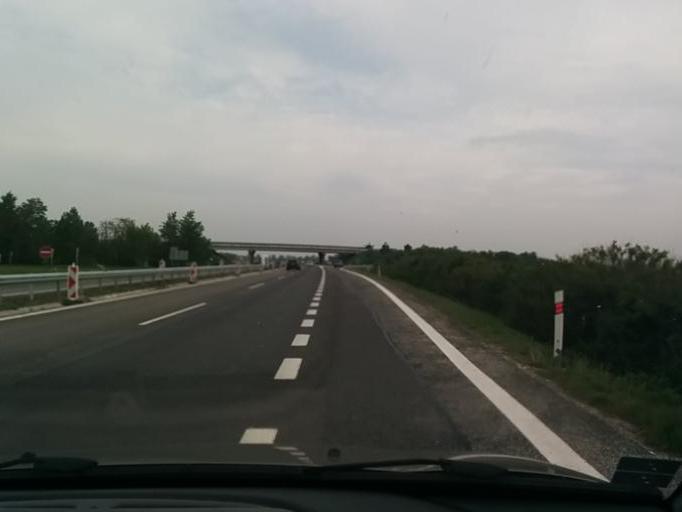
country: SK
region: Trnavsky
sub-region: Okres Galanta
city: Galanta
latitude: 48.2728
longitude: 17.7176
